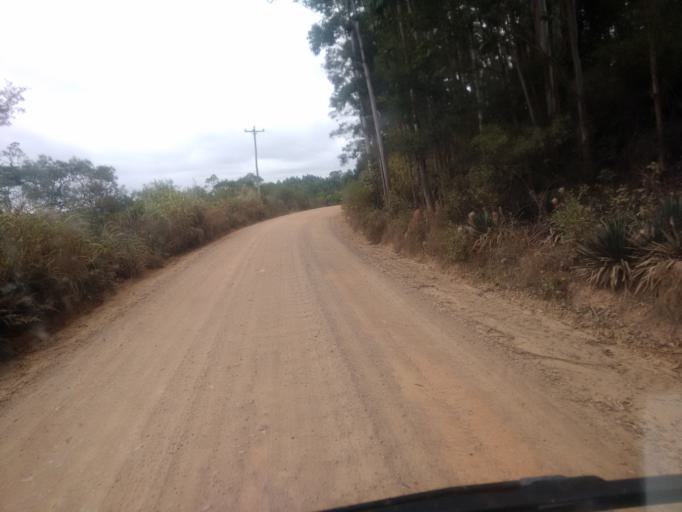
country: BR
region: Rio Grande do Sul
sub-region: Camaqua
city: Camaqua
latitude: -30.7572
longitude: -51.8770
